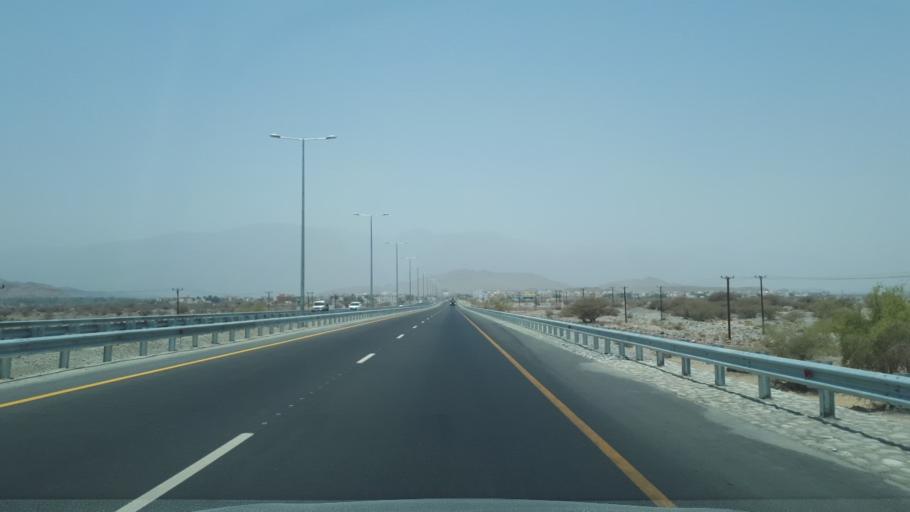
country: OM
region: Al Batinah
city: Rustaq
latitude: 23.4663
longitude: 57.4418
